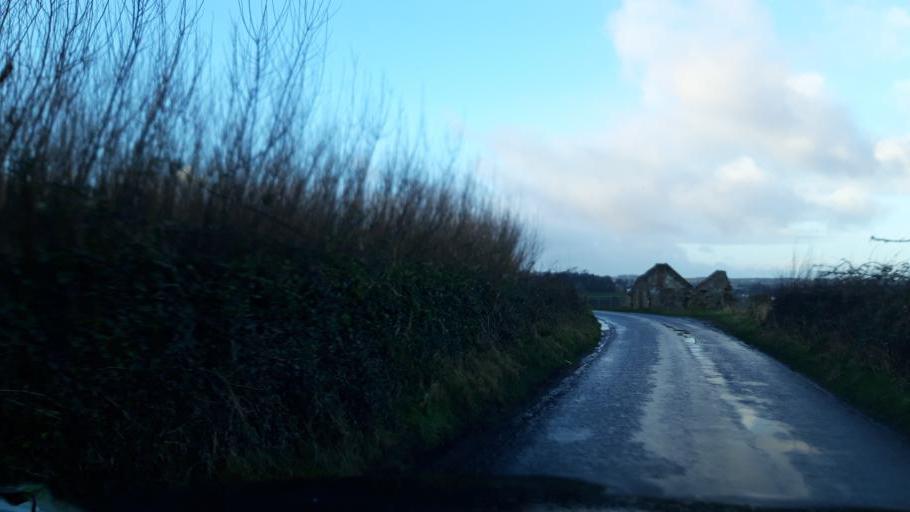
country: GB
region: Northern Ireland
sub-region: Moyle District
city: Ballycastle
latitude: 55.1978
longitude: -6.2189
